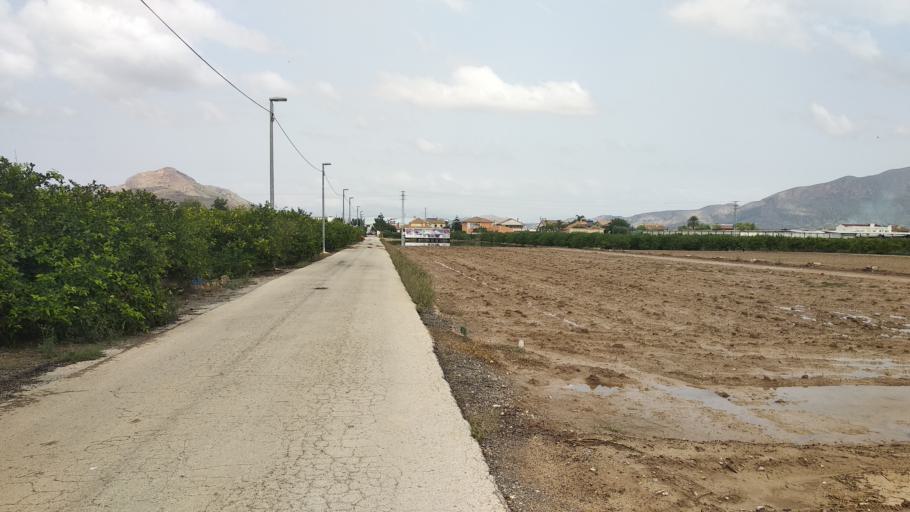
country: ES
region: Murcia
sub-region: Murcia
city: Santomera
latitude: 38.0402
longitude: -1.0402
